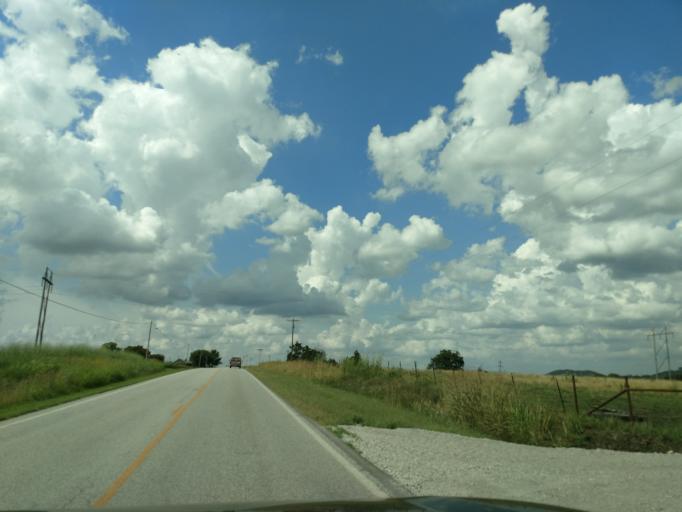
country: US
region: Arkansas
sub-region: Carroll County
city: Berryville
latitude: 36.4547
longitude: -93.5559
